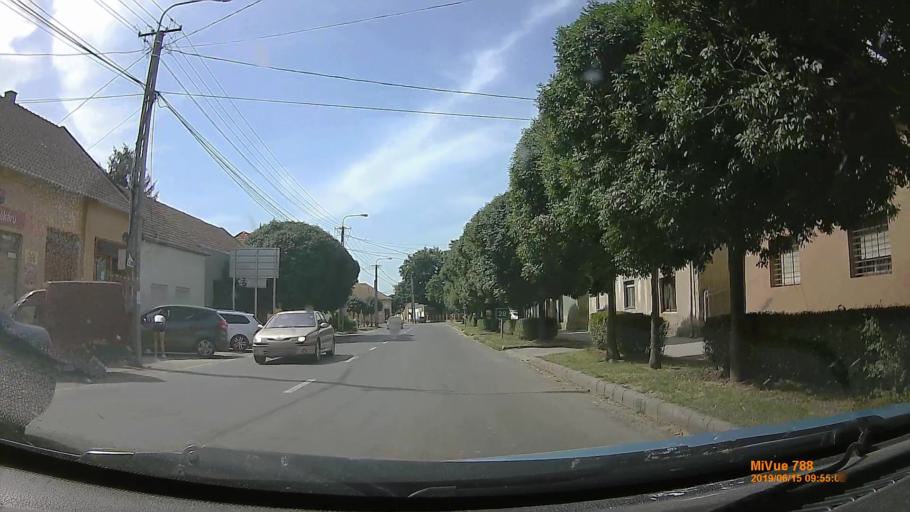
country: HU
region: Baranya
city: Sasd
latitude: 46.2538
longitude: 18.1064
